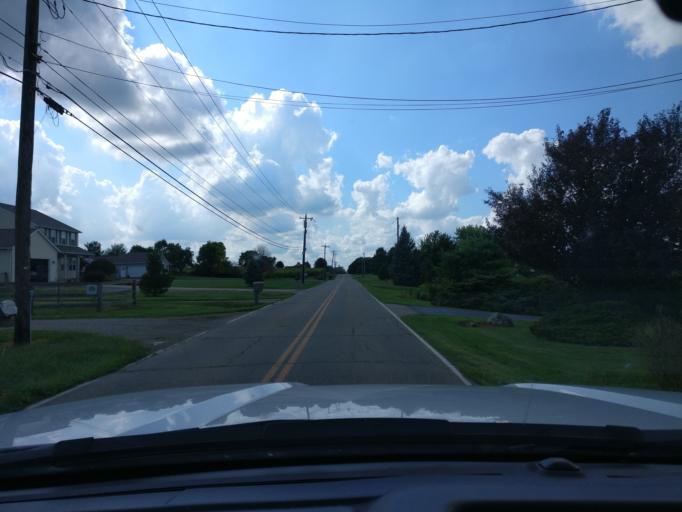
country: US
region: Ohio
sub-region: Warren County
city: Springboro
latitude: 39.5034
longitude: -84.2044
